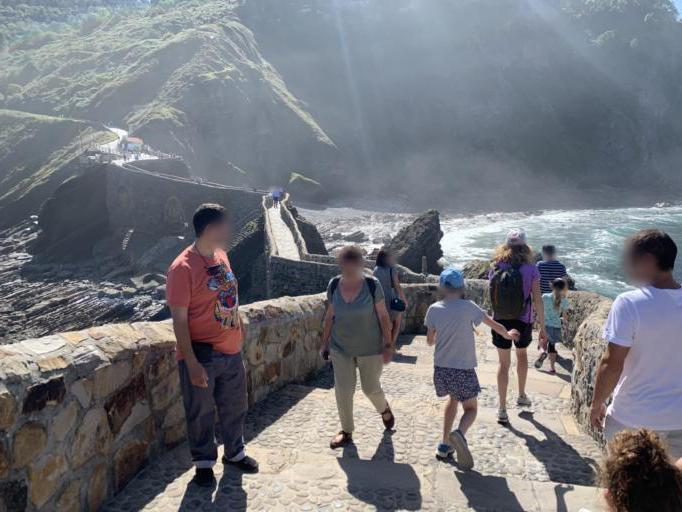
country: ES
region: Basque Country
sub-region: Bizkaia
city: Bakio
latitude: 43.4462
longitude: -2.7846
